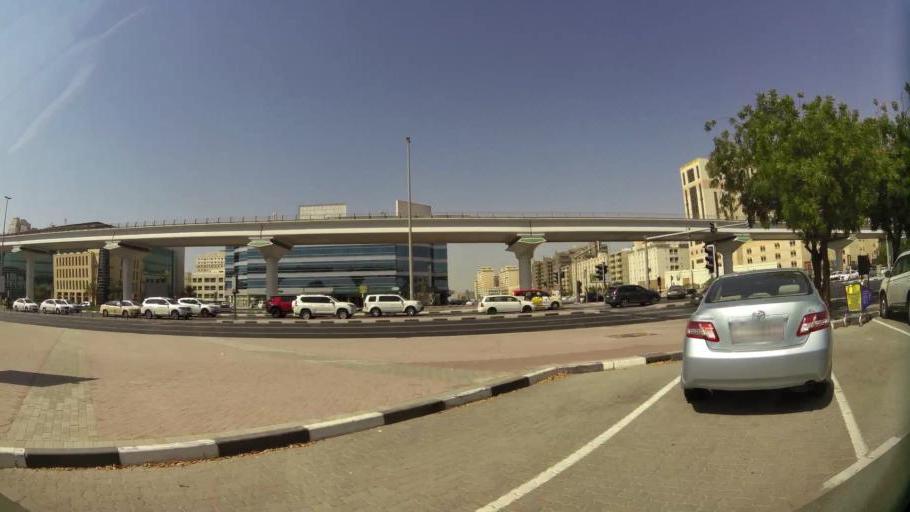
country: AE
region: Ash Shariqah
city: Sharjah
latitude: 25.2715
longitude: 55.3713
